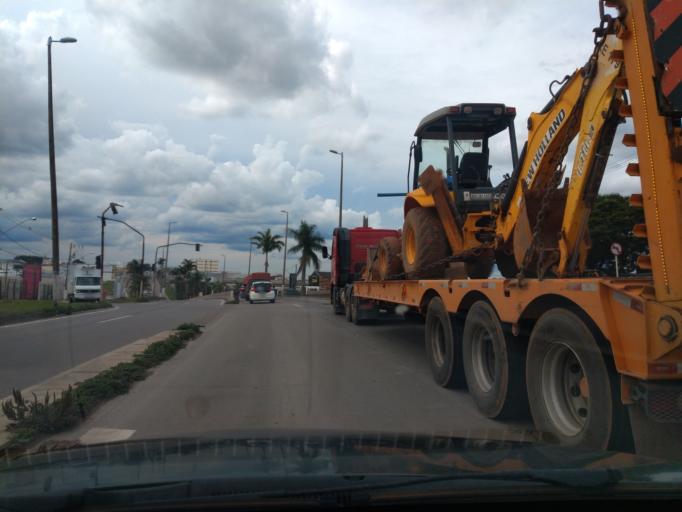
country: BR
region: Minas Gerais
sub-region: Varginha
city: Varginha
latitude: -21.5889
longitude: -45.4375
